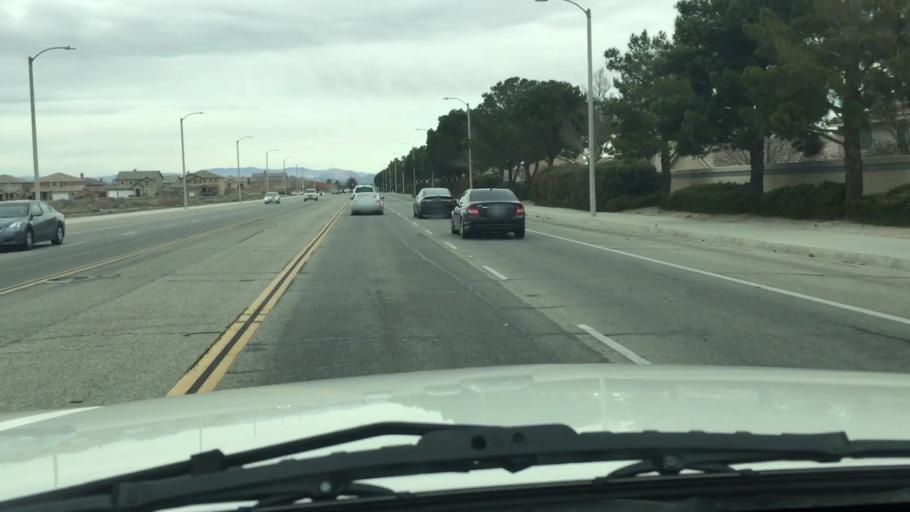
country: US
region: California
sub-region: Los Angeles County
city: Lancaster
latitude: 34.6906
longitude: -118.1838
